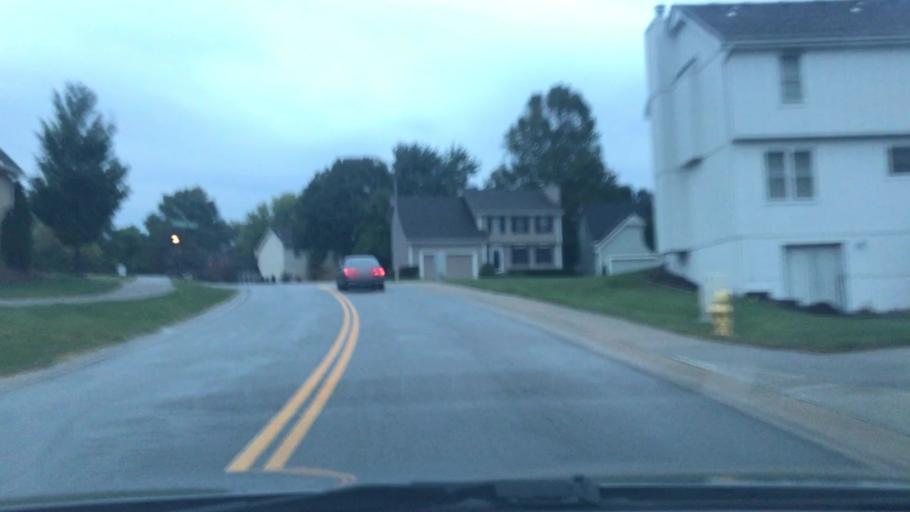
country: US
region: Missouri
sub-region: Jackson County
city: Blue Springs
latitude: 39.0009
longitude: -94.3583
